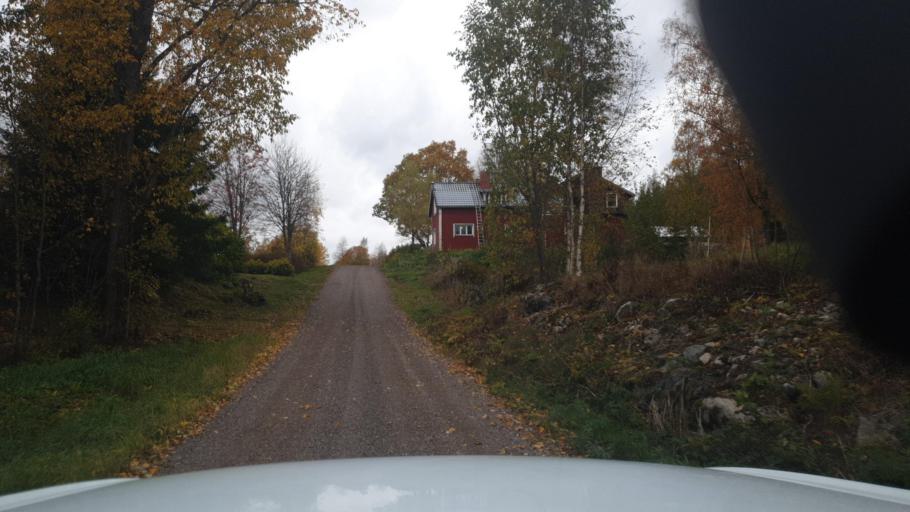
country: SE
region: Vaermland
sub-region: Arvika Kommun
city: Arvika
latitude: 59.9562
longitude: 12.7268
